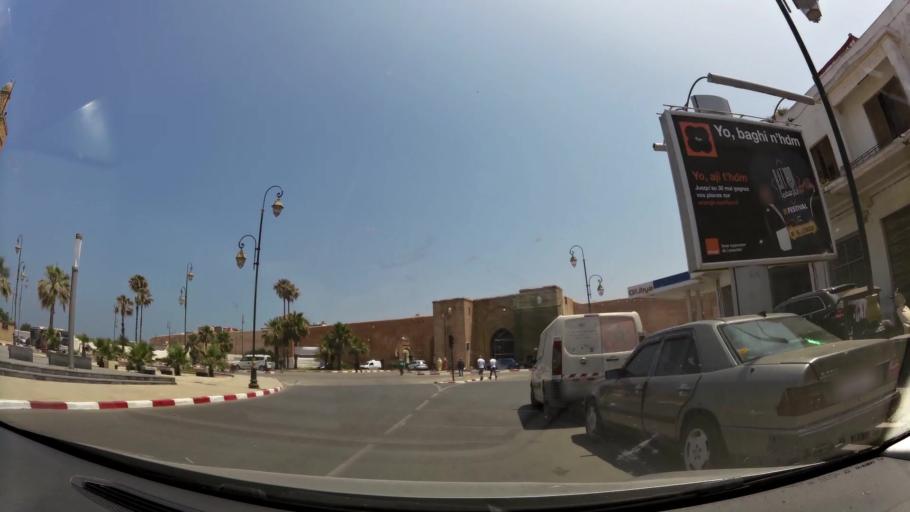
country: MA
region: Rabat-Sale-Zemmour-Zaer
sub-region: Rabat
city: Rabat
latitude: 34.0263
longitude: -6.8425
